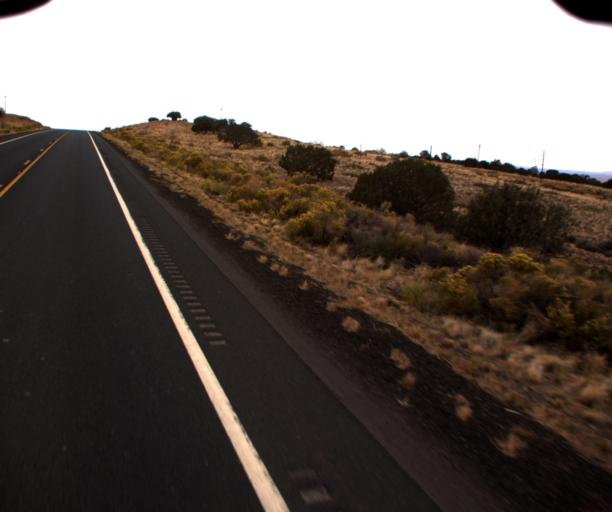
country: US
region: Arizona
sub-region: Coconino County
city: Kaibito
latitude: 36.4481
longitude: -110.7231
